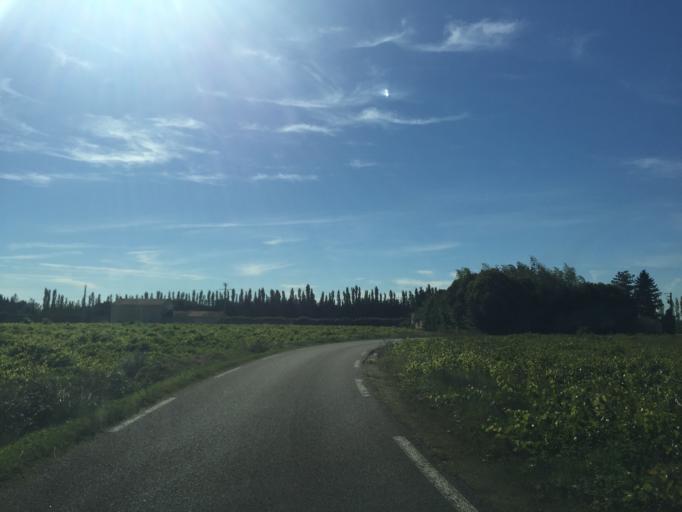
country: FR
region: Provence-Alpes-Cote d'Azur
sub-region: Departement du Vaucluse
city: Orange
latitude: 44.1396
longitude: 4.7703
